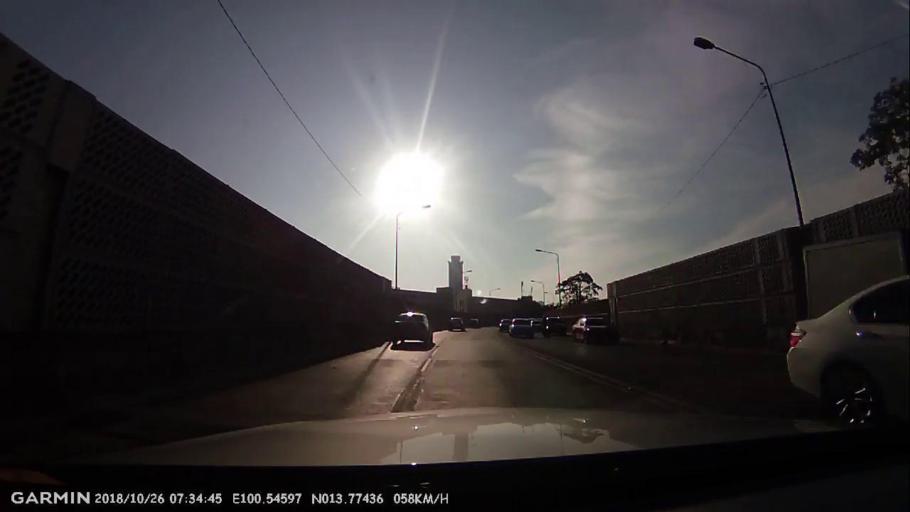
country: TH
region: Bangkok
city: Phaya Thai
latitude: 13.7743
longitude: 100.5460
